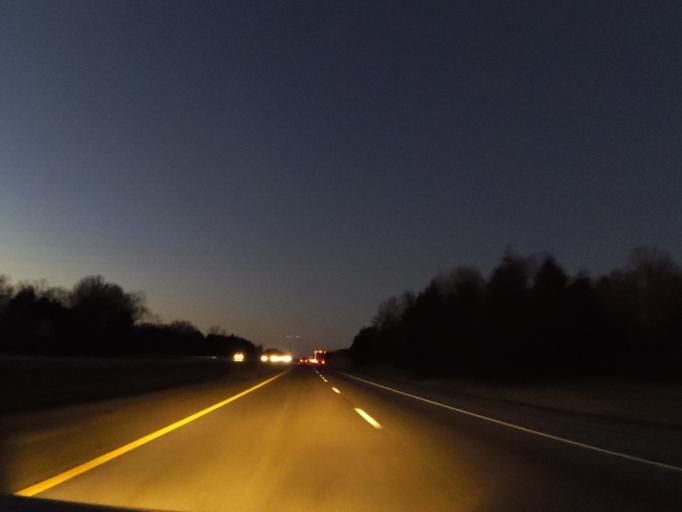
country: US
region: Tennessee
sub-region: Cocke County
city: Newport
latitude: 35.9986
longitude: -83.2879
